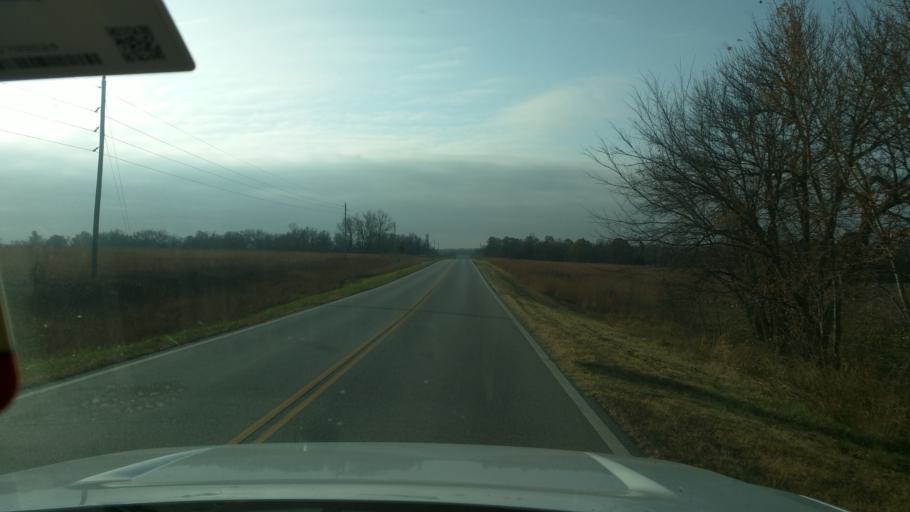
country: US
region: Kansas
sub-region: Greenwood County
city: Eureka
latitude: 37.7592
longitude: -96.2345
